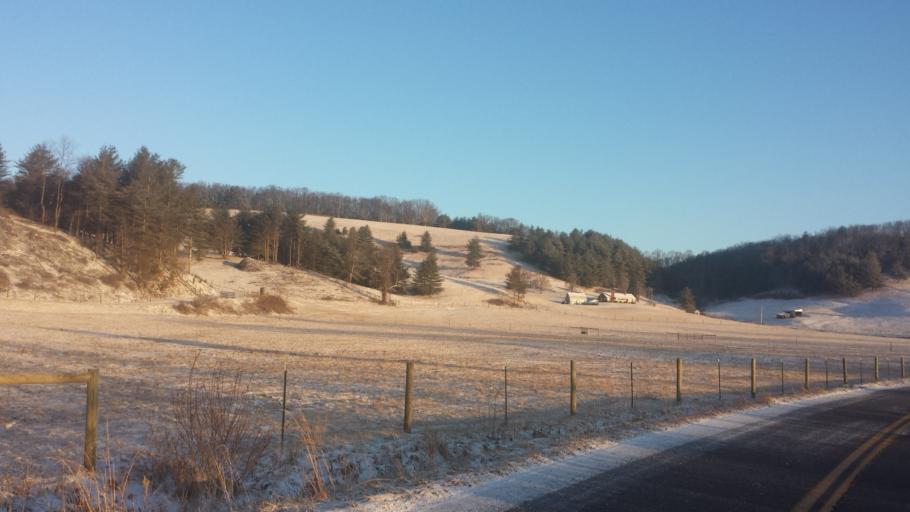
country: US
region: Virginia
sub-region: Franklin County
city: Ferrum
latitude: 36.9715
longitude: -80.1420
